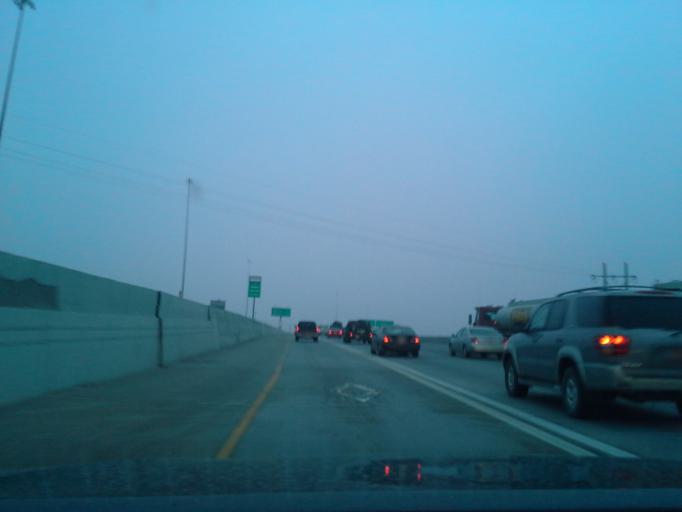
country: US
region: Utah
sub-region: Salt Lake County
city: Midvale
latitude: 40.6322
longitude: -111.9047
